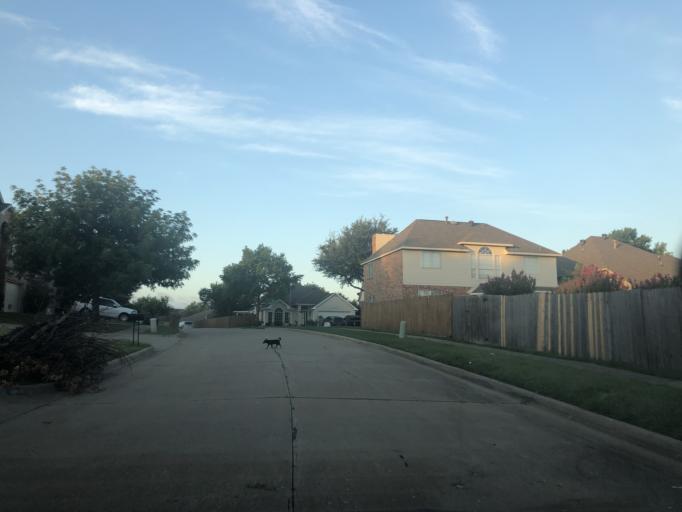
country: US
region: Texas
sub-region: Dallas County
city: Cedar Hill
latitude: 32.6503
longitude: -96.9730
